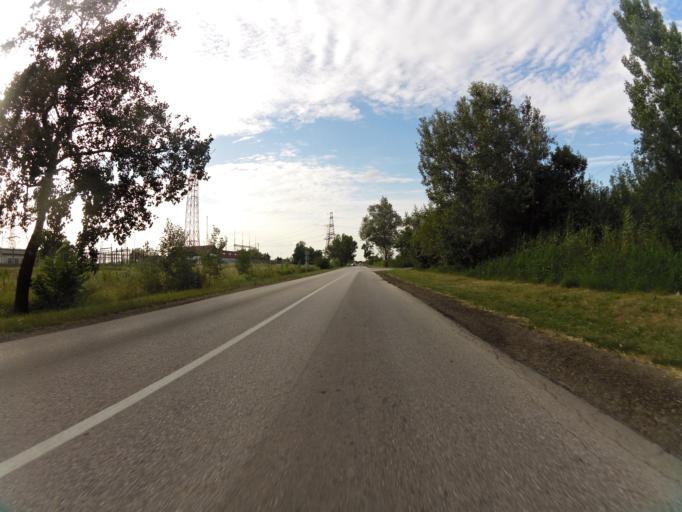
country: HU
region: Csongrad
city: Szeged
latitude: 46.3042
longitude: 20.1309
